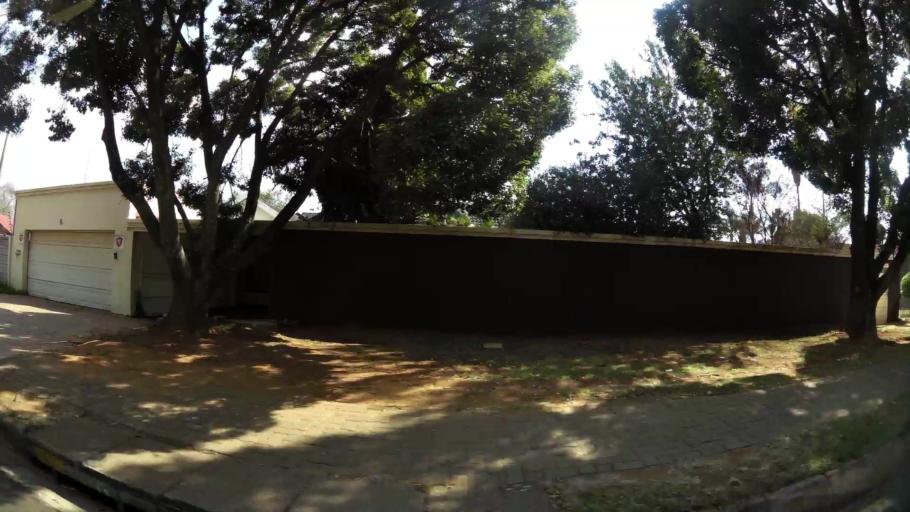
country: ZA
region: Gauteng
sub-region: City of Johannesburg Metropolitan Municipality
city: Modderfontein
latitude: -26.0781
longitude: 28.2364
